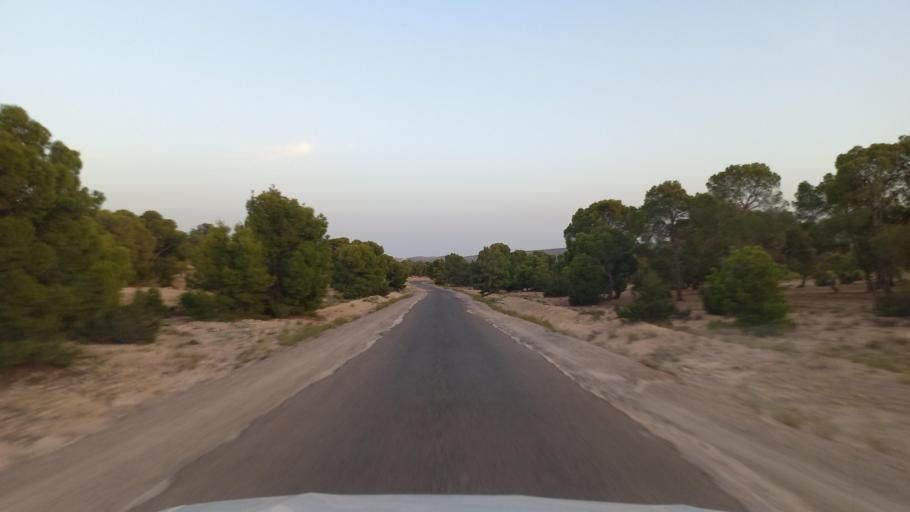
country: TN
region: Al Qasrayn
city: Sbiba
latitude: 35.4236
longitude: 8.9223
